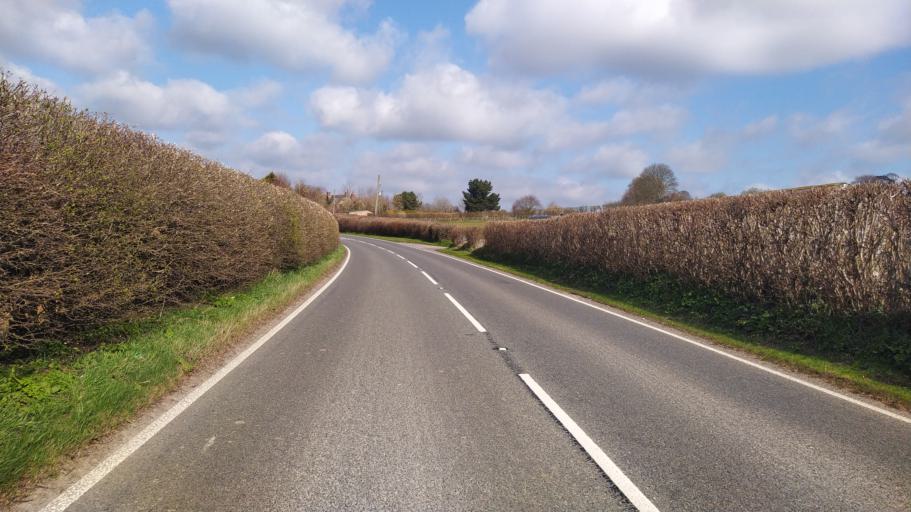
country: GB
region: England
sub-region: Dorset
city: Beaminster
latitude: 50.7715
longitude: -2.7323
